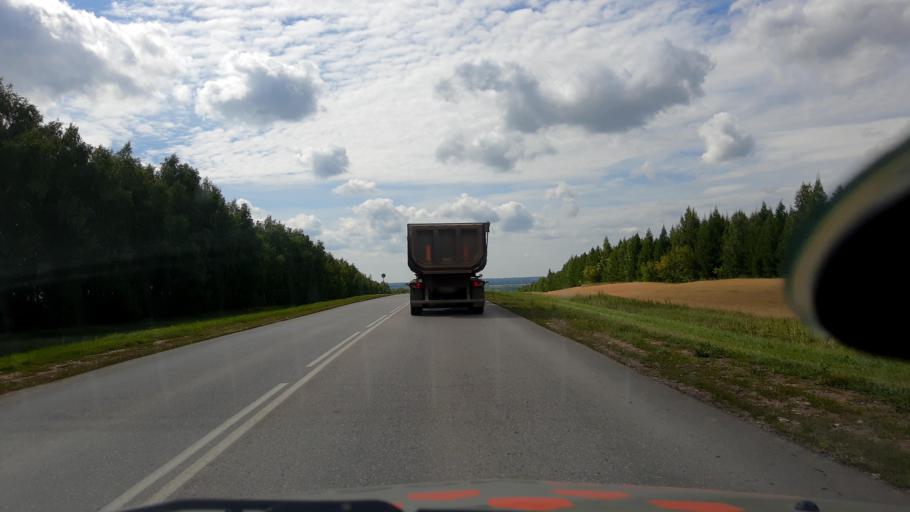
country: RU
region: Bashkortostan
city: Buzdyak
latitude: 54.7053
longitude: 54.5648
